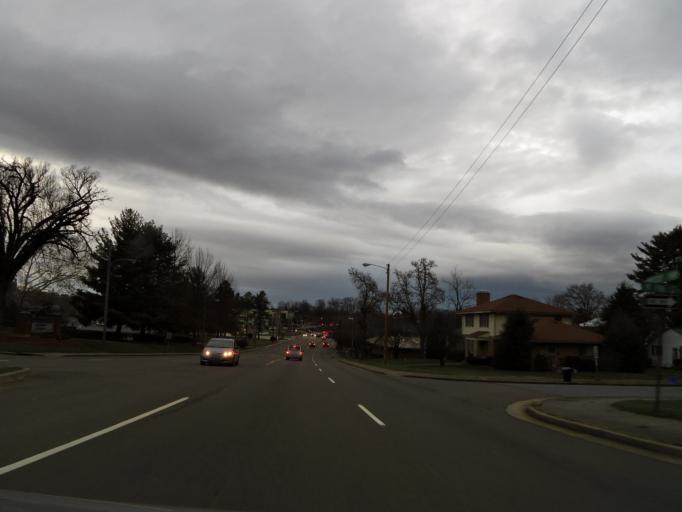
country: US
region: Tennessee
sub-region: Washington County
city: Johnson City
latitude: 36.3051
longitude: -82.3634
